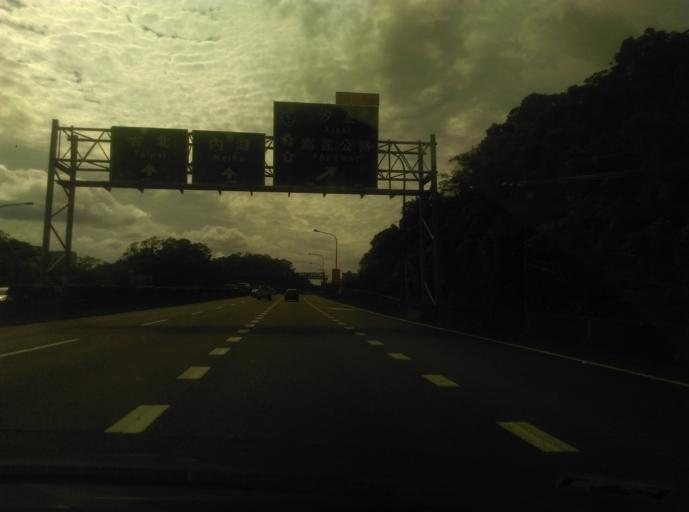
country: TW
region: Taiwan
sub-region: Keelung
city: Keelung
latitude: 25.0774
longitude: 121.6613
